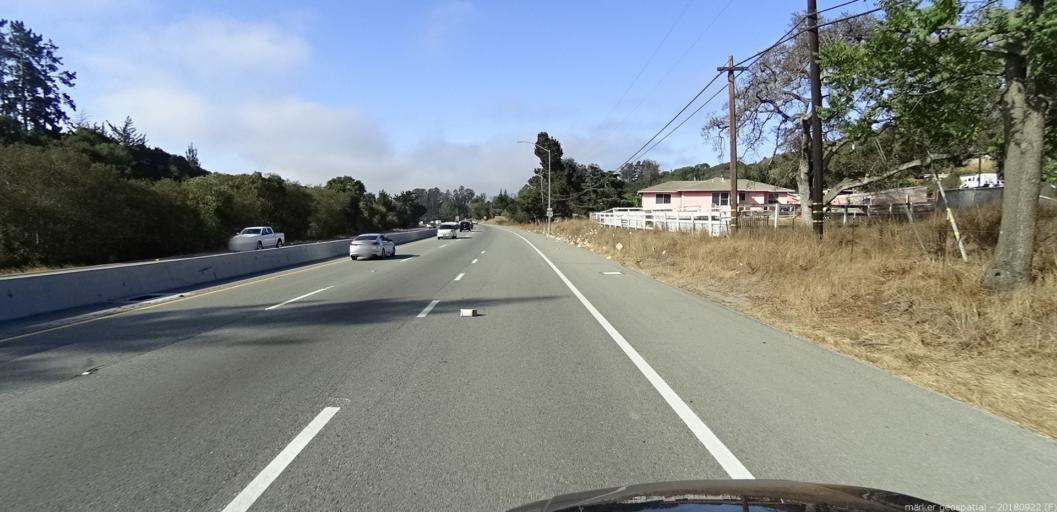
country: US
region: California
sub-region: Monterey County
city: Prunedale
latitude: 36.8154
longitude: -121.6399
